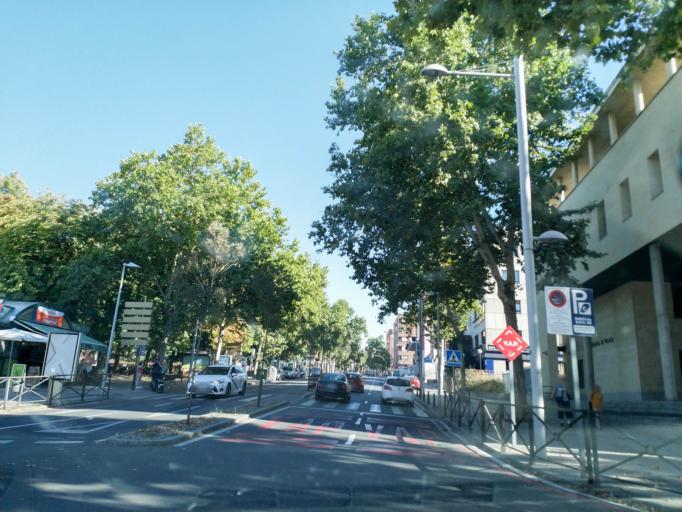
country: ES
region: Castille and Leon
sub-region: Provincia de Segovia
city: Segovia
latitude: 40.9446
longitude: -4.1213
